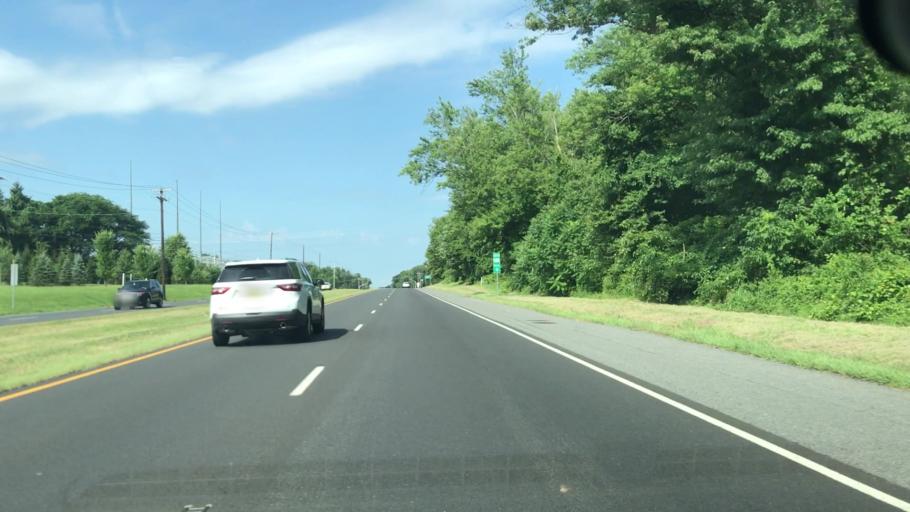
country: US
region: New Jersey
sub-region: Hunterdon County
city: Whitehouse Station
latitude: 40.5469
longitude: -74.7421
